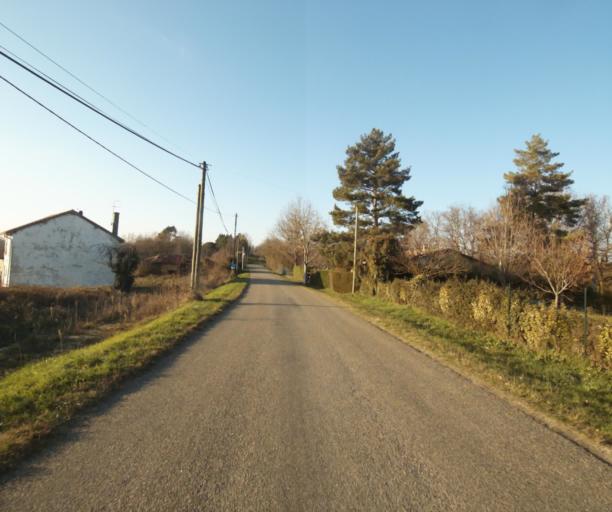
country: FR
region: Midi-Pyrenees
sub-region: Departement du Tarn-et-Garonne
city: Moissac
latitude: 44.1366
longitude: 1.1235
